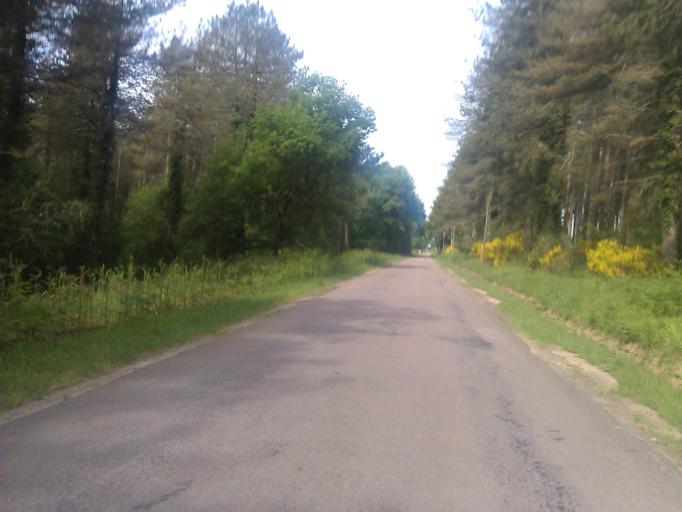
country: FR
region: Auvergne
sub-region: Departement de l'Allier
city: Vallon-en-Sully
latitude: 46.6133
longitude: 2.6727
